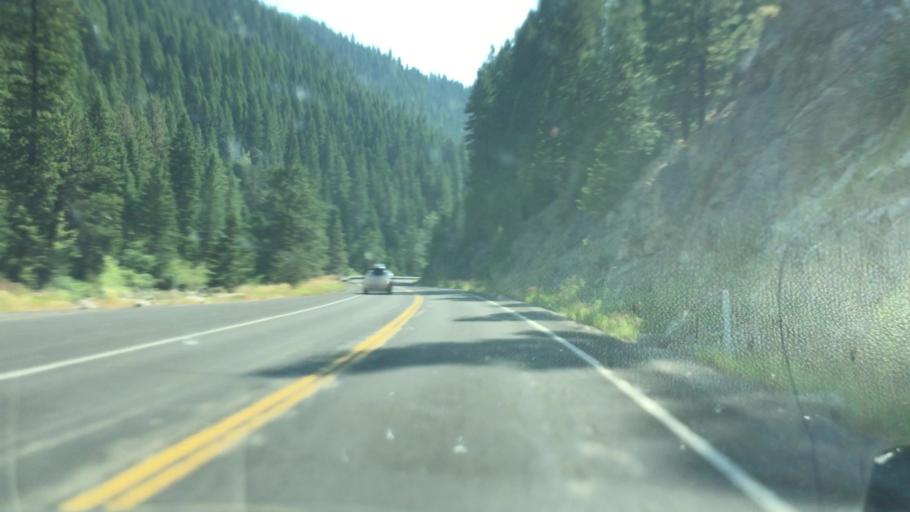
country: US
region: Idaho
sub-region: Valley County
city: Cascade
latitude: 44.2576
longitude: -116.0822
